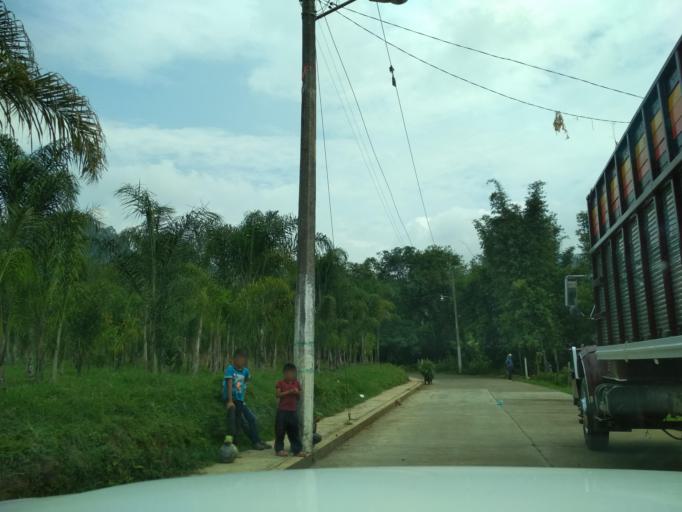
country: MX
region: Veracruz
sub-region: La Perla
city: La Perla
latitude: 18.9282
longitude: -97.1291
